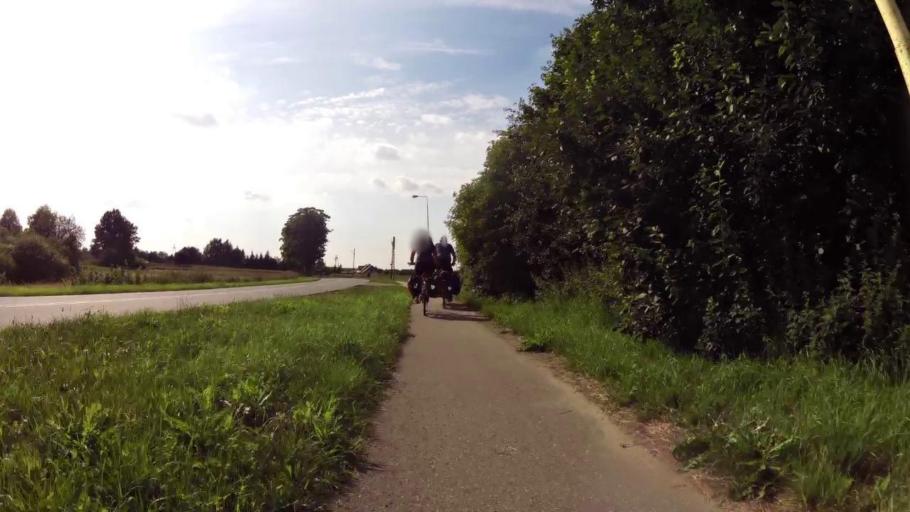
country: PL
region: West Pomeranian Voivodeship
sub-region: Powiat lobeski
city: Wegorzyno
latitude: 53.5515
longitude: 15.5406
